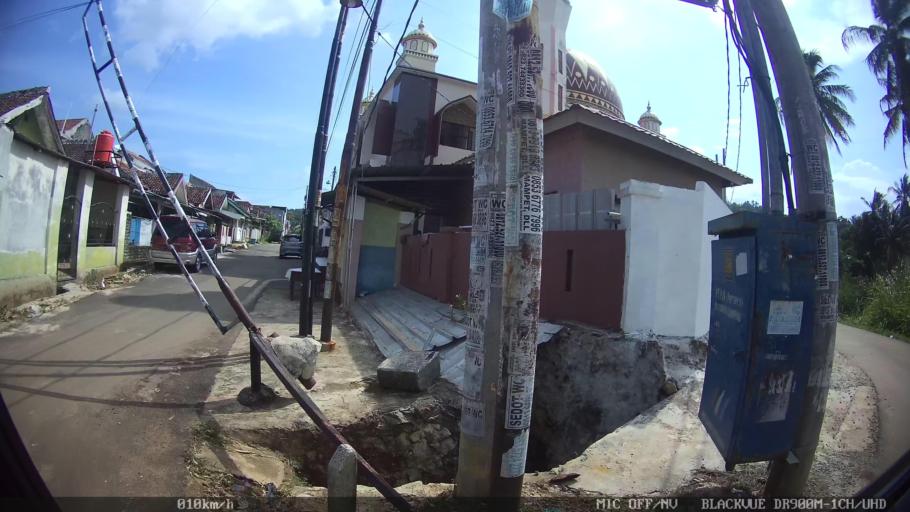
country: ID
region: Lampung
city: Kedaton
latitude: -5.3990
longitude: 105.2287
